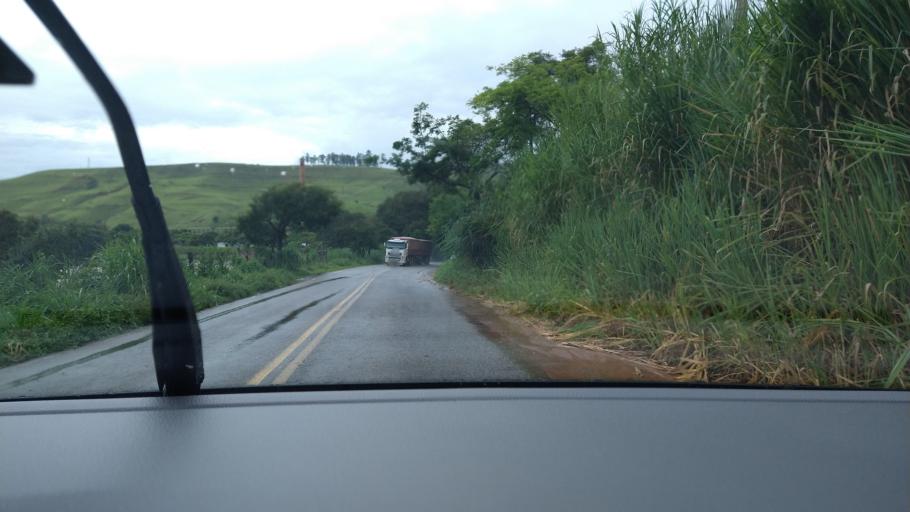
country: BR
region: Minas Gerais
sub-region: Ponte Nova
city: Ponte Nova
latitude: -20.3740
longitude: -42.8957
